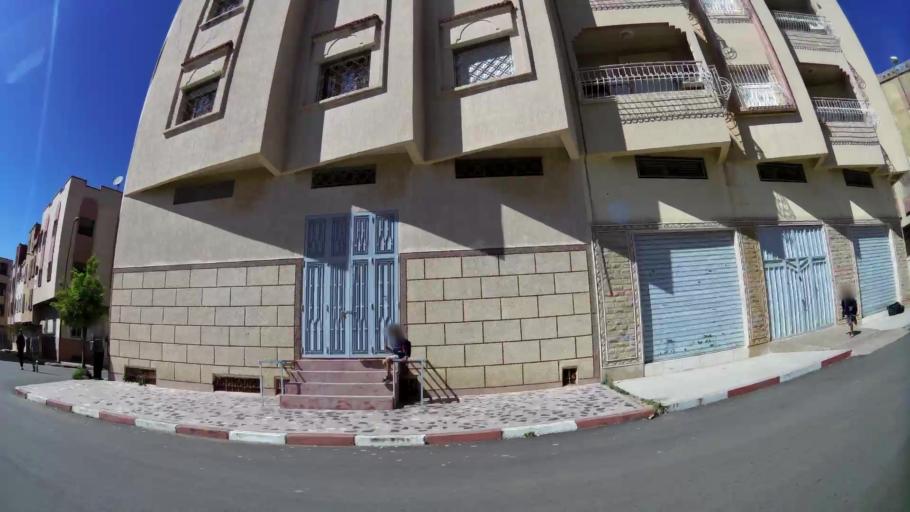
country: MA
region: Meknes-Tafilalet
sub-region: Meknes
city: Meknes
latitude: 33.8846
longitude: -5.5797
